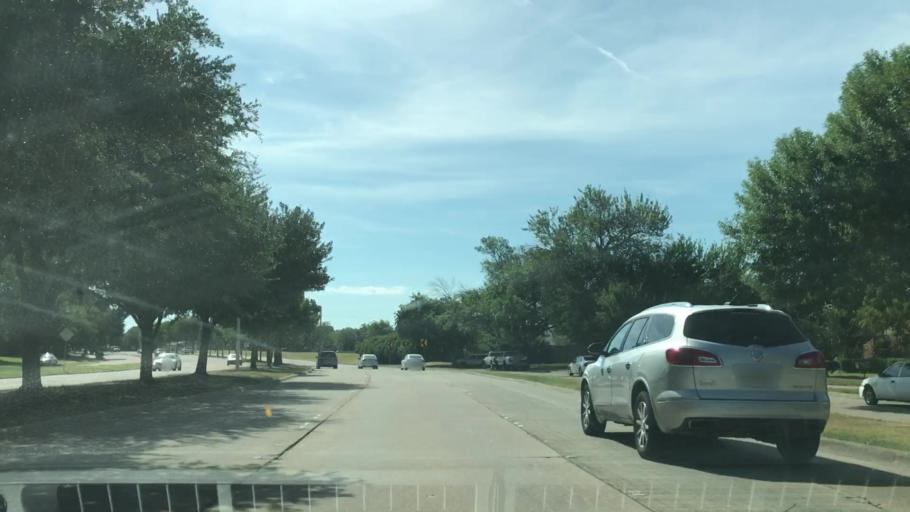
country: US
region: Texas
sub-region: Collin County
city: Plano
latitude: 33.0565
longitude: -96.7270
